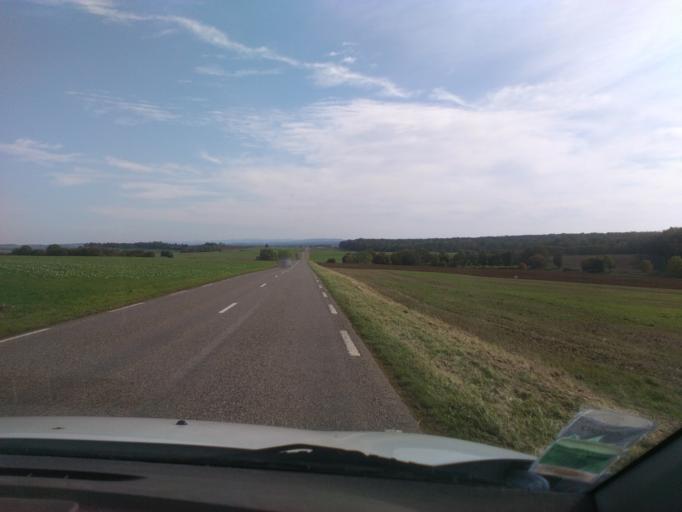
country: FR
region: Lorraine
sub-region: Departement des Vosges
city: Rambervillers
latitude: 48.3526
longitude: 6.5465
